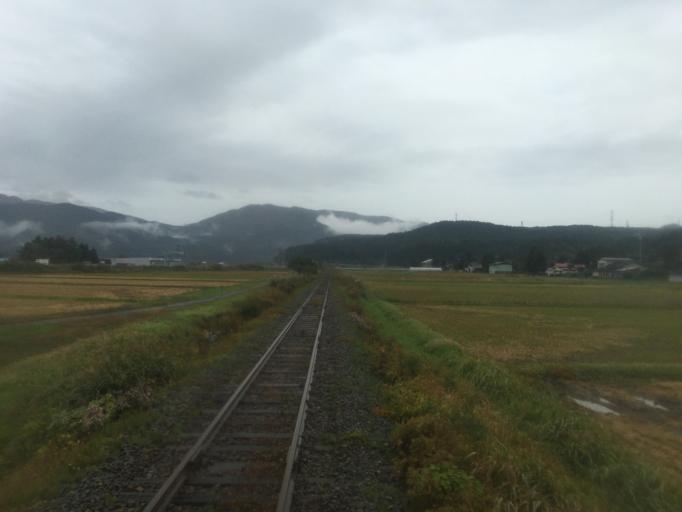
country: JP
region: Yamagata
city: Tsuruoka
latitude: 38.7909
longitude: 139.9893
